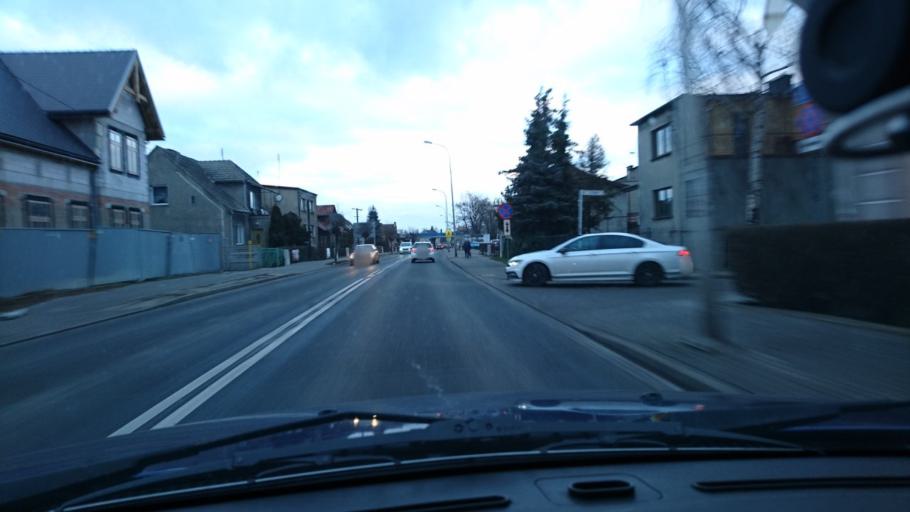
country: PL
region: Greater Poland Voivodeship
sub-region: Powiat kepinski
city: Kepno
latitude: 51.2860
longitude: 17.9930
